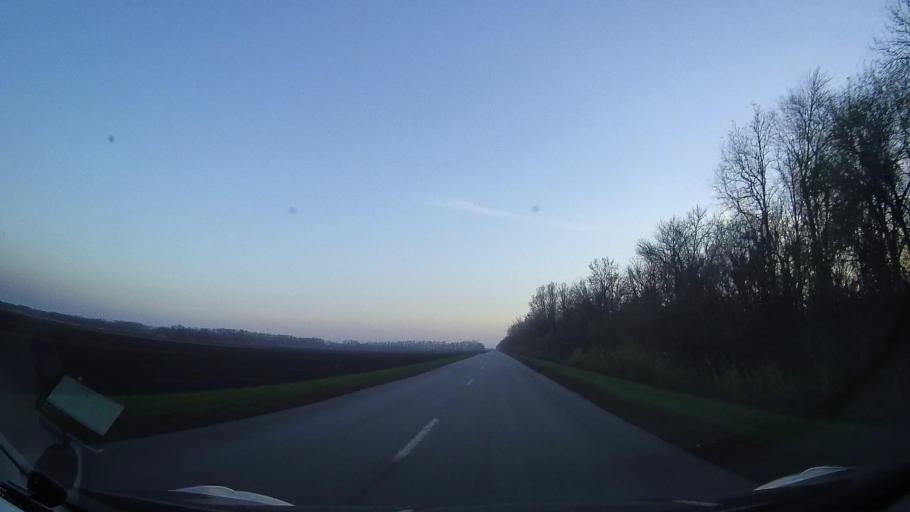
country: RU
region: Rostov
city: Zernograd
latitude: 46.9988
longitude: 40.3915
